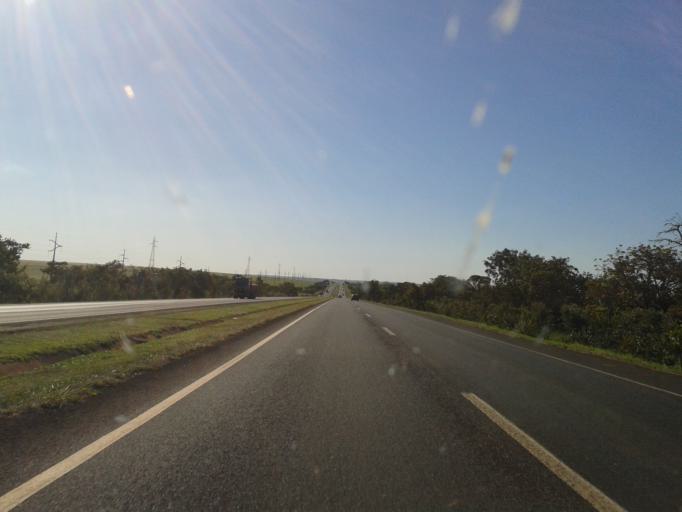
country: BR
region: Minas Gerais
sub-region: Uberlandia
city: Uberlandia
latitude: -19.0651
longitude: -48.1919
